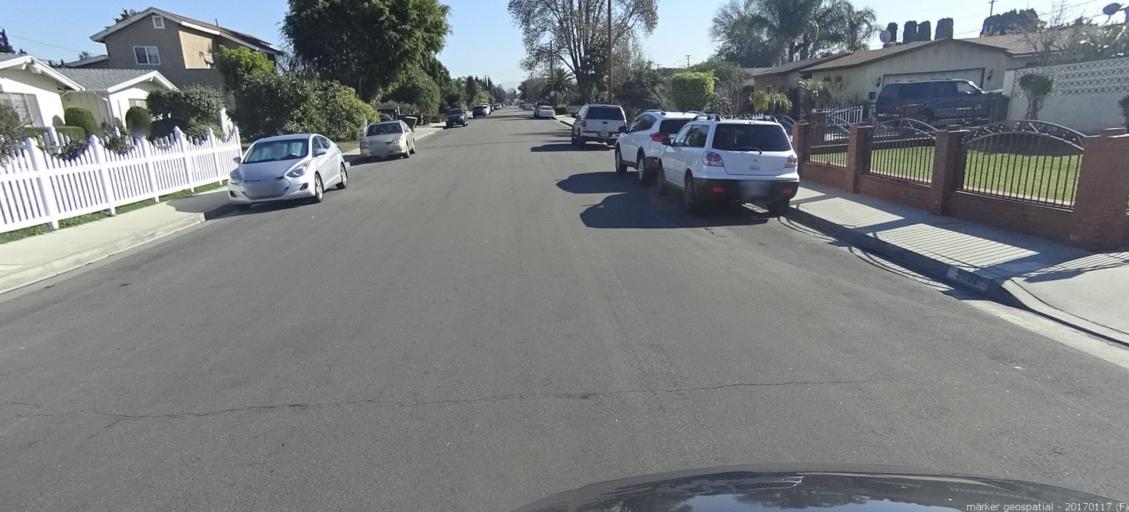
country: US
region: California
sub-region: Orange County
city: Stanton
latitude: 33.8096
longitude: -117.9654
